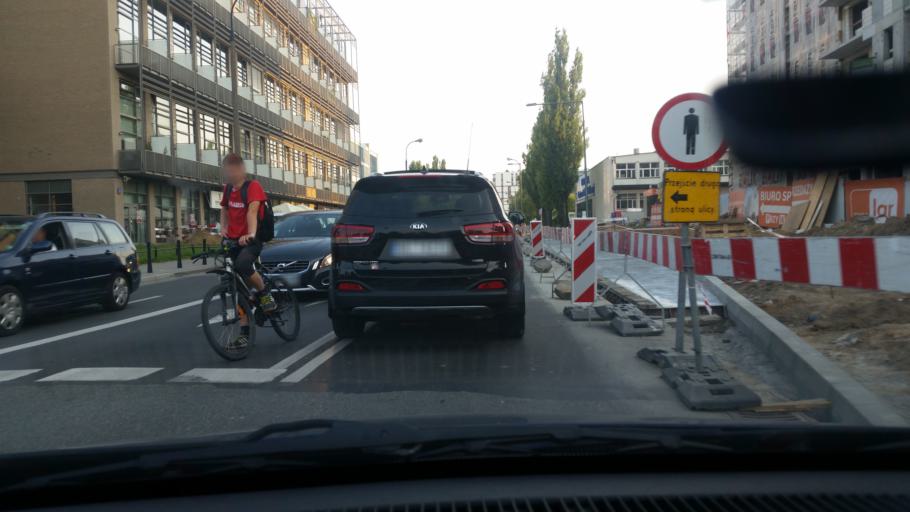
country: PL
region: Masovian Voivodeship
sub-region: Warszawa
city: Ochota
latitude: 52.1887
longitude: 20.9927
